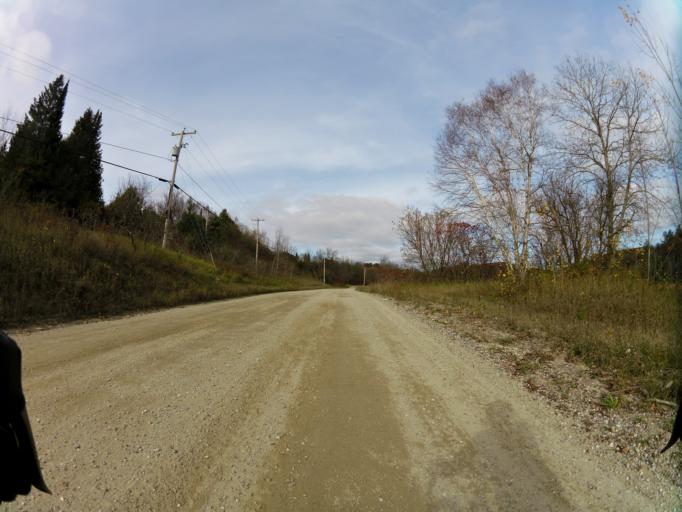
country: CA
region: Quebec
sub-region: Outaouais
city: Wakefield
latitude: 45.7409
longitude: -75.9723
